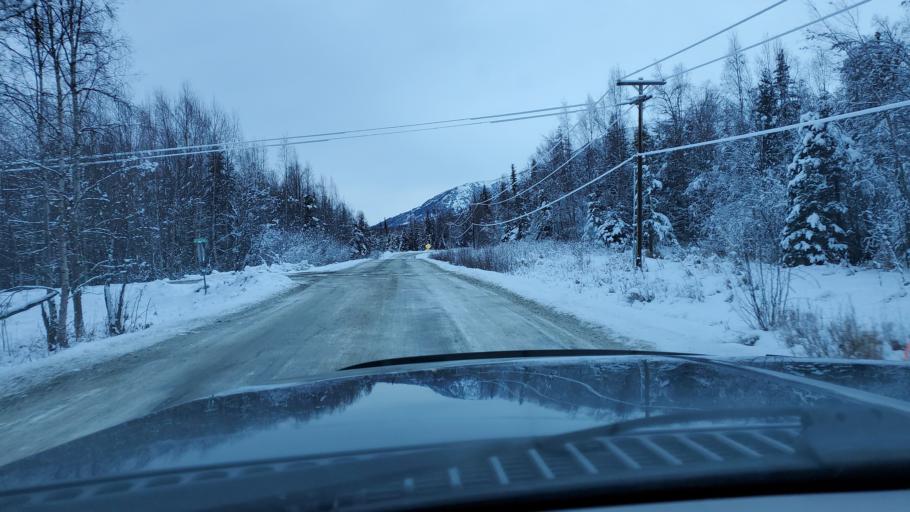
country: US
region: Alaska
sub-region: Matanuska-Susitna Borough
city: Lakes
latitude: 61.6933
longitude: -149.3181
